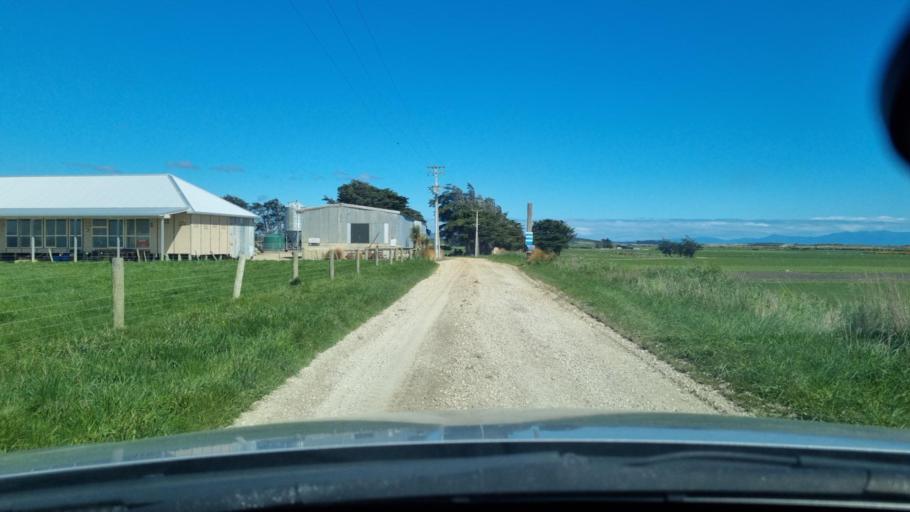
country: NZ
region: Southland
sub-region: Invercargill City
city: Invercargill
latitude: -46.3999
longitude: 168.2562
